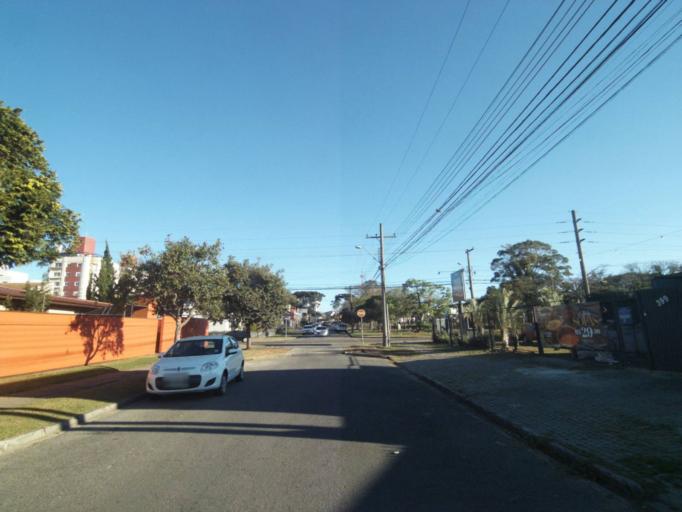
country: BR
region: Parana
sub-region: Curitiba
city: Curitiba
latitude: -25.4597
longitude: -49.3012
